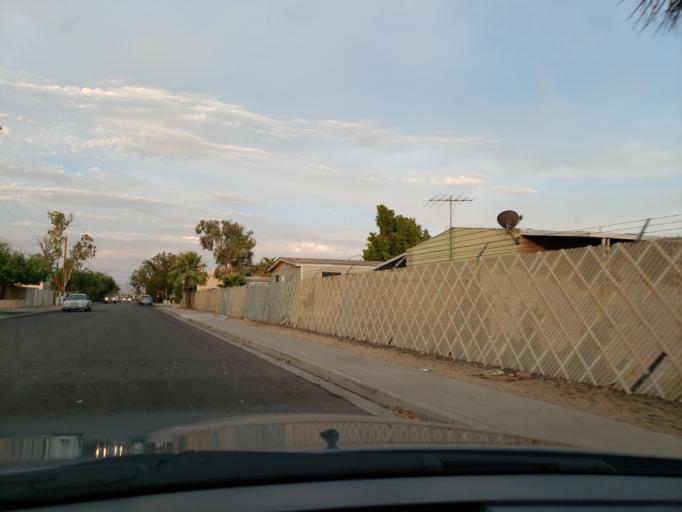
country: US
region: Arizona
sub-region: Maricopa County
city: Paradise Valley
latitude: 33.6353
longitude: -112.0187
